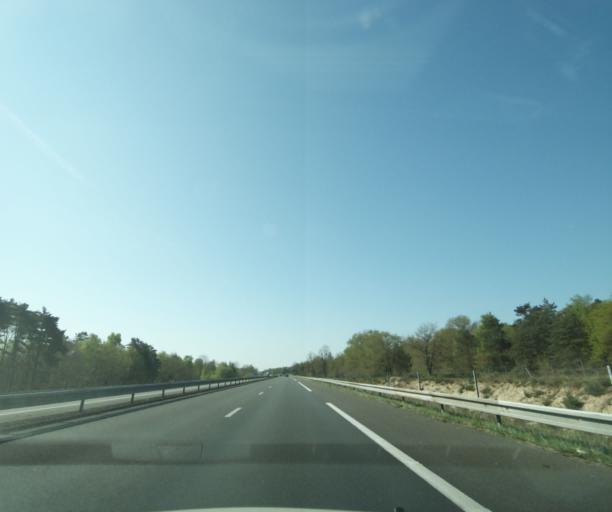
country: FR
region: Centre
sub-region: Departement du Loiret
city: Saint-Hilaire-Saint-Mesmin
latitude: 47.8350
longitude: 1.8625
